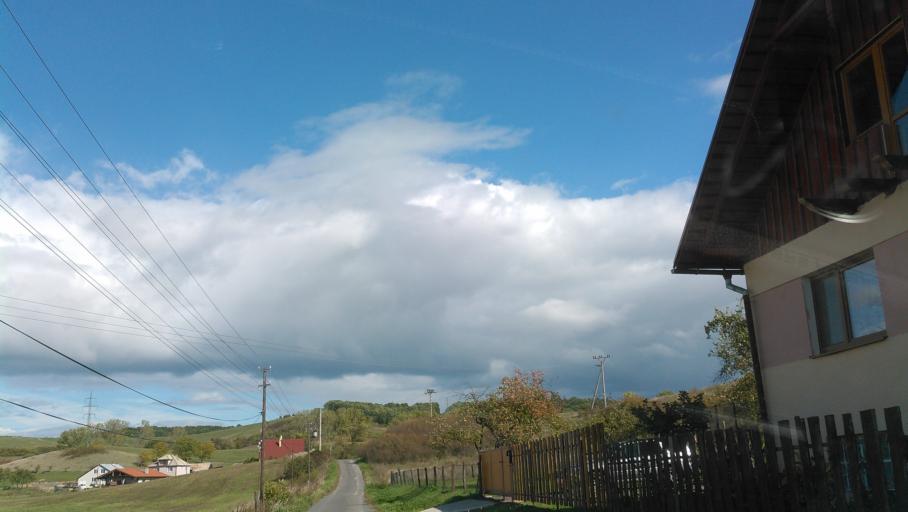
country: SK
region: Banskobystricky
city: Poltar
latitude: 48.3851
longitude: 19.9005
